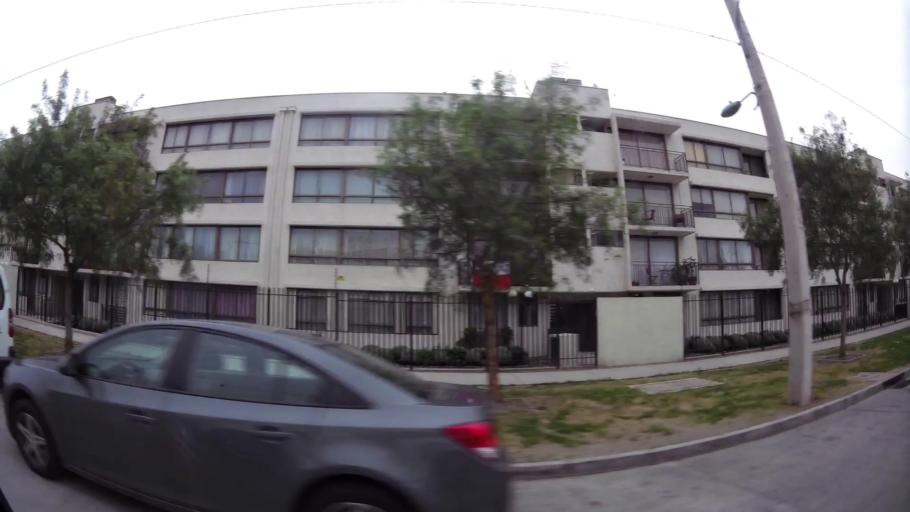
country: CL
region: Santiago Metropolitan
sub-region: Provincia de Santiago
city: Lo Prado
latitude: -33.5222
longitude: -70.7687
